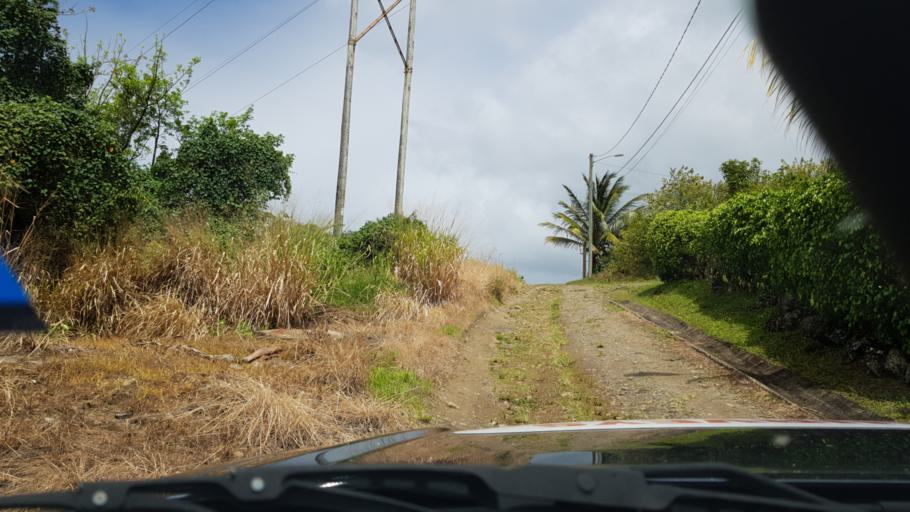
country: LC
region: Anse-la-Raye
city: Anse La Raye
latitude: 13.9459
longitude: -61.0312
